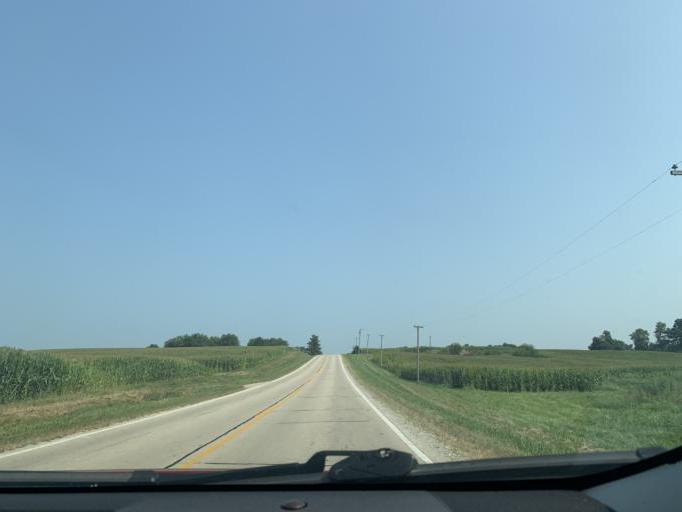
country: US
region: Illinois
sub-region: Whiteside County
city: Sterling
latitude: 41.8447
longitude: -89.8045
